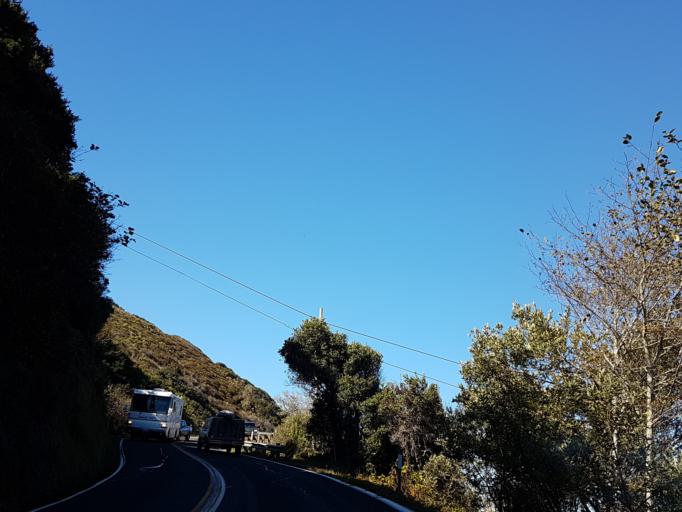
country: US
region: California
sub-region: Mendocino County
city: Boonville
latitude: 39.1011
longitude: -123.7047
